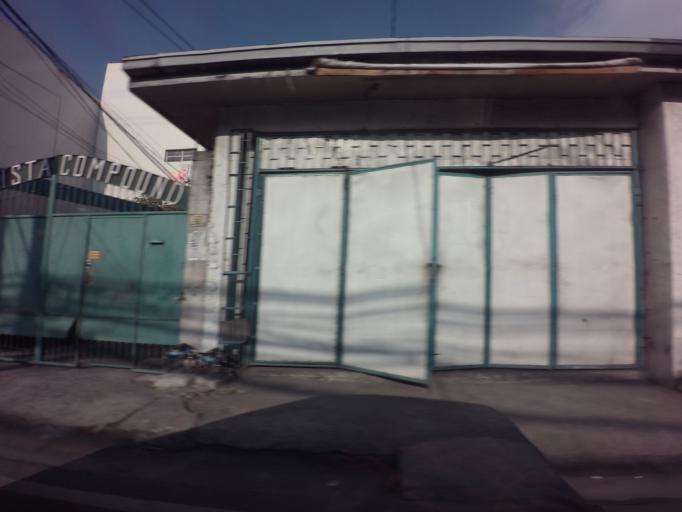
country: PH
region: Calabarzon
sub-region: Province of Rizal
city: Taguig
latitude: 14.4816
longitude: 121.0612
